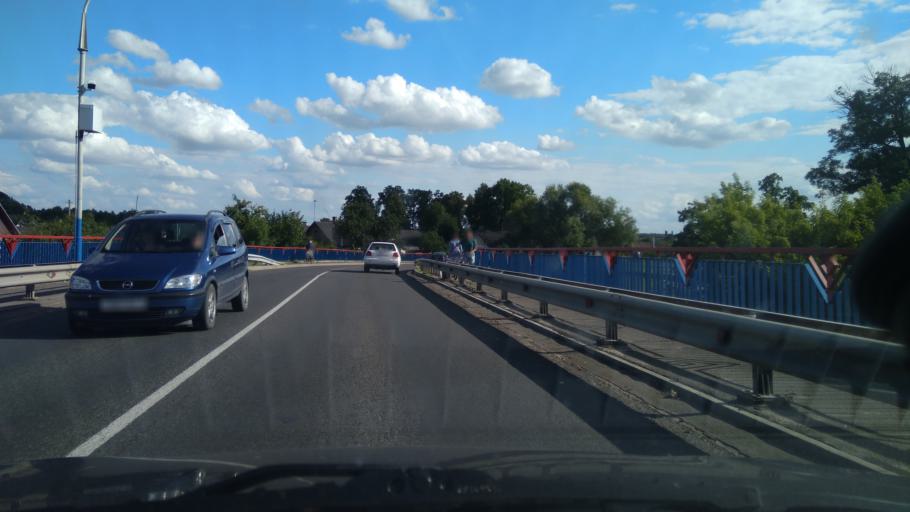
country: BY
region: Grodnenskaya
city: Masty
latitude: 53.4043
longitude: 24.5356
